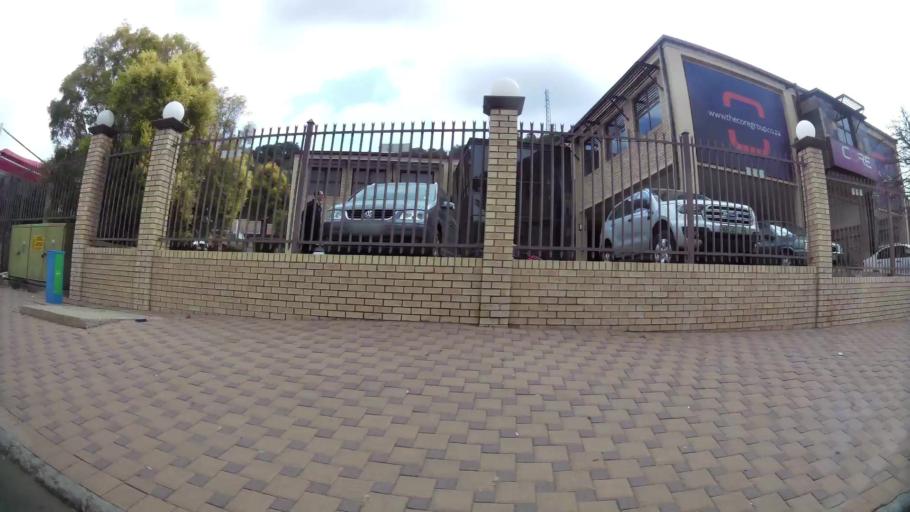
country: ZA
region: Orange Free State
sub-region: Mangaung Metropolitan Municipality
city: Bloemfontein
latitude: -29.1088
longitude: 26.2177
